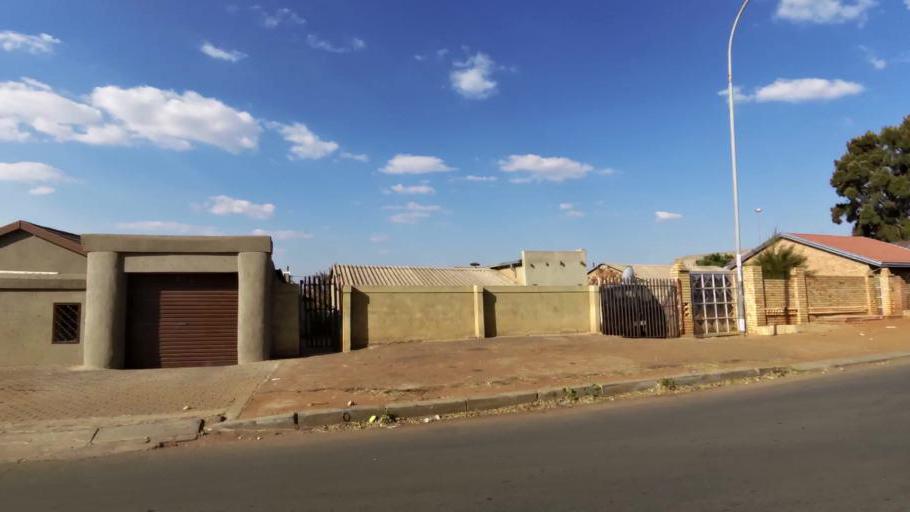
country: ZA
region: Gauteng
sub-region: City of Johannesburg Metropolitan Municipality
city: Soweto
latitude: -26.2263
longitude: 27.8733
